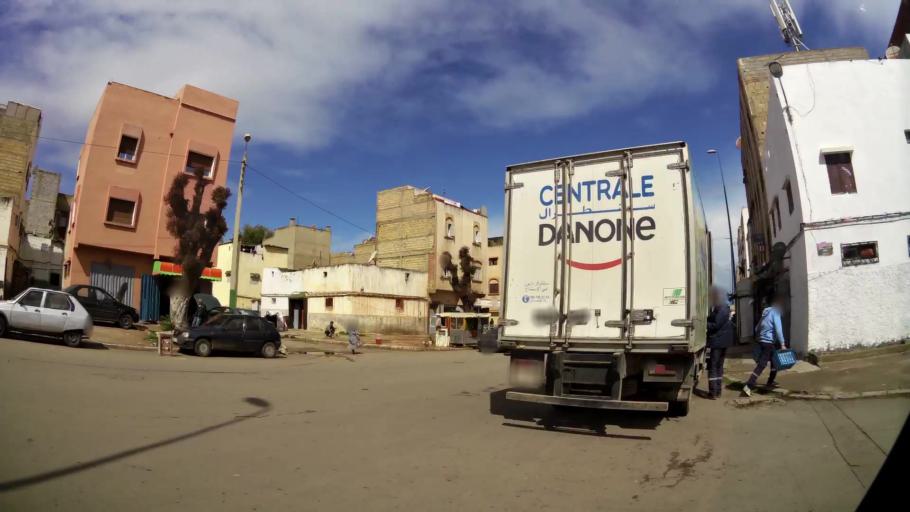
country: MA
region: Grand Casablanca
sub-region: Casablanca
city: Casablanca
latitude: 33.5717
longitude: -7.6846
